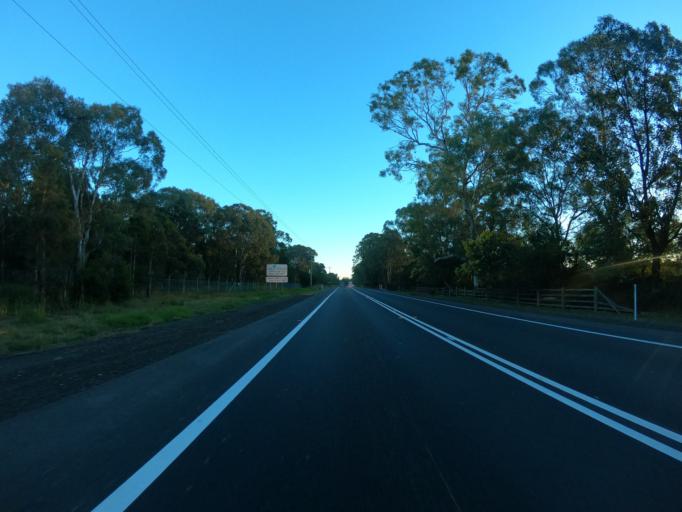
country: AU
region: New South Wales
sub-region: Hawkesbury
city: South Windsor
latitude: -33.6565
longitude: 150.7947
